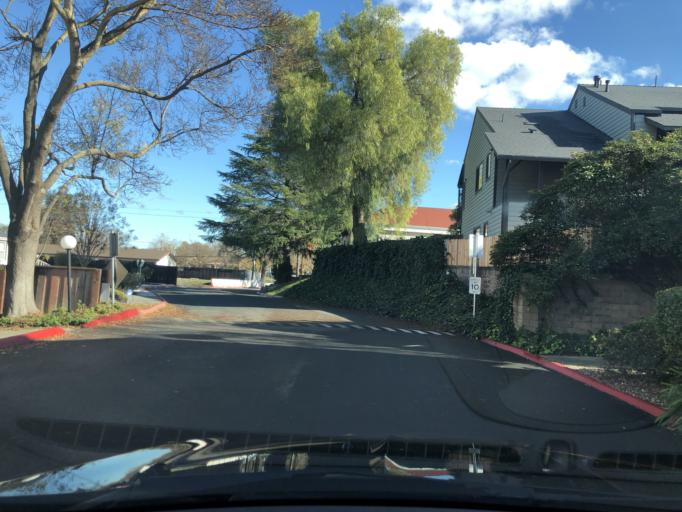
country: US
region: California
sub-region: Contra Costa County
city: Pacheco
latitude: 37.9841
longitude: -122.0705
